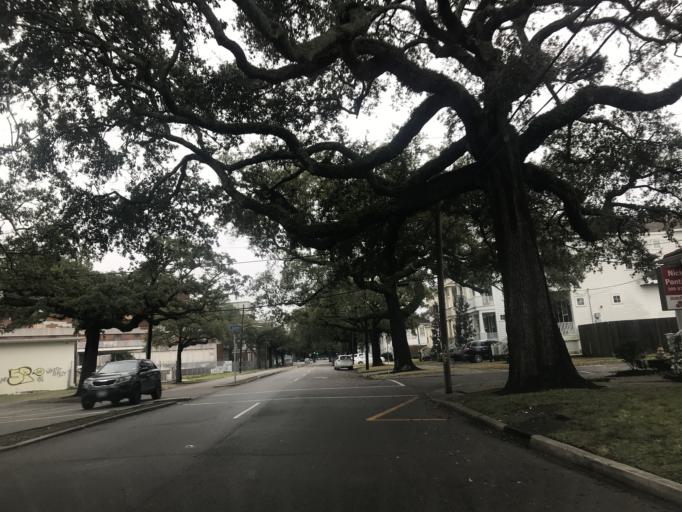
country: US
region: Louisiana
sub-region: Orleans Parish
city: New Orleans
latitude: 29.9732
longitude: -90.0948
